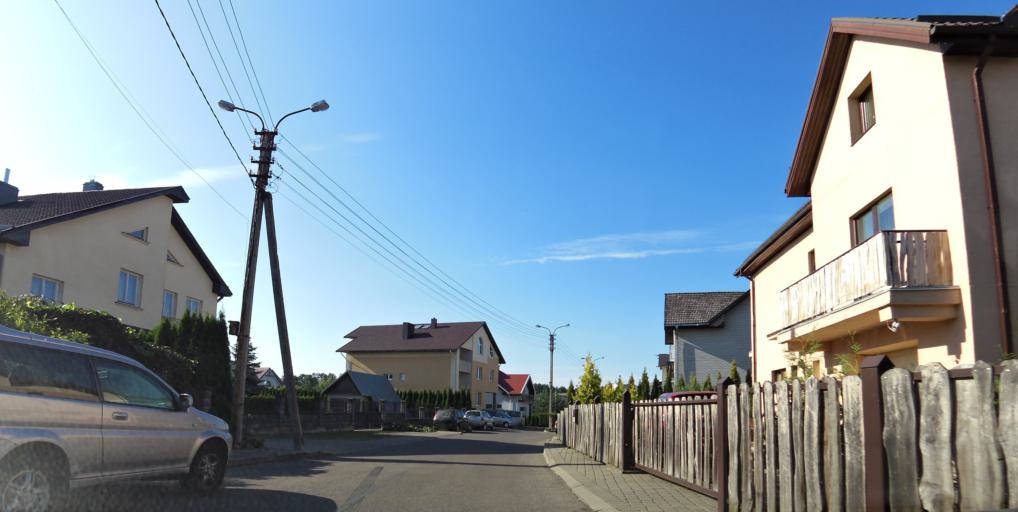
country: LT
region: Vilnius County
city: Pilaite
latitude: 54.7118
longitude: 25.1929
